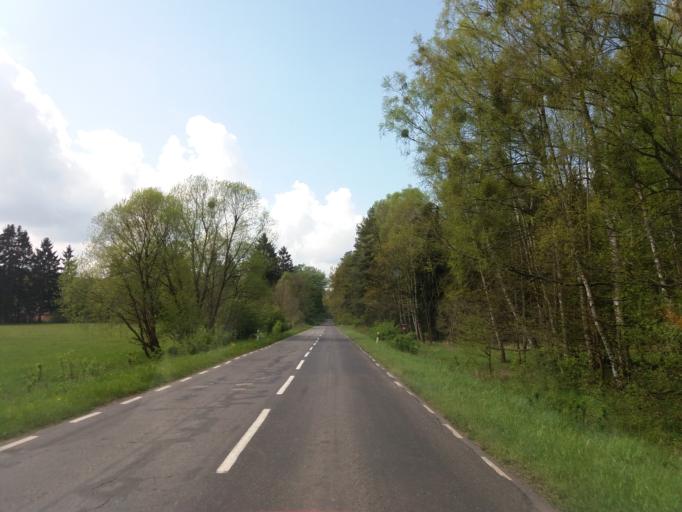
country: PL
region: West Pomeranian Voivodeship
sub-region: Powiat choszczenski
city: Drawno
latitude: 53.2385
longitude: 15.8143
